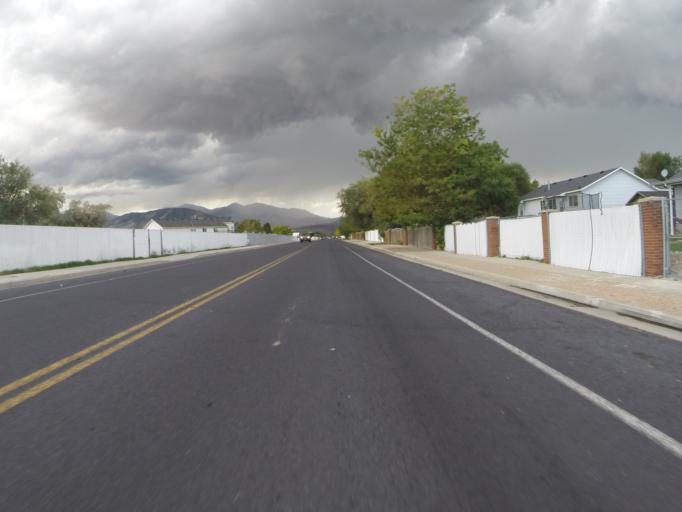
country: US
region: Utah
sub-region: Salt Lake County
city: West Valley City
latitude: 40.7038
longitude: -112.0447
